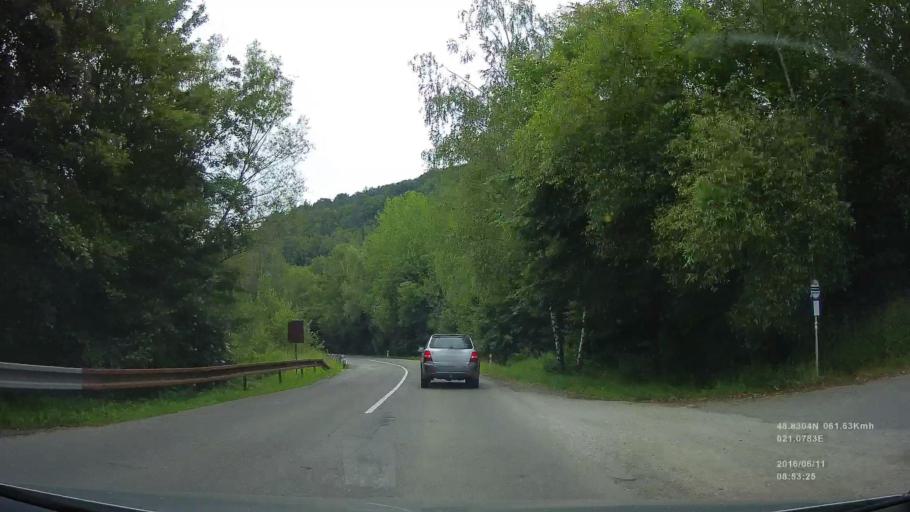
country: SK
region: Kosicky
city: Gelnica
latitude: 48.8256
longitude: 21.0816
